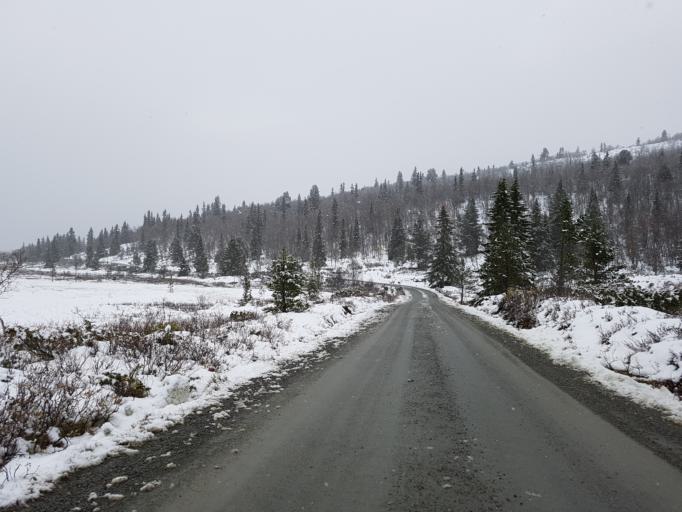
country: NO
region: Oppland
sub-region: Sel
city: Otta
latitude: 61.7958
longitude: 9.7145
